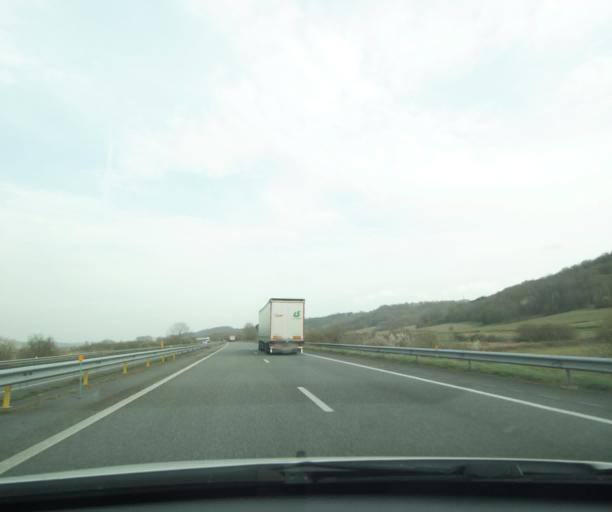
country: FR
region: Aquitaine
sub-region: Departement des Landes
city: Labatut
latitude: 43.5185
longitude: -0.9727
